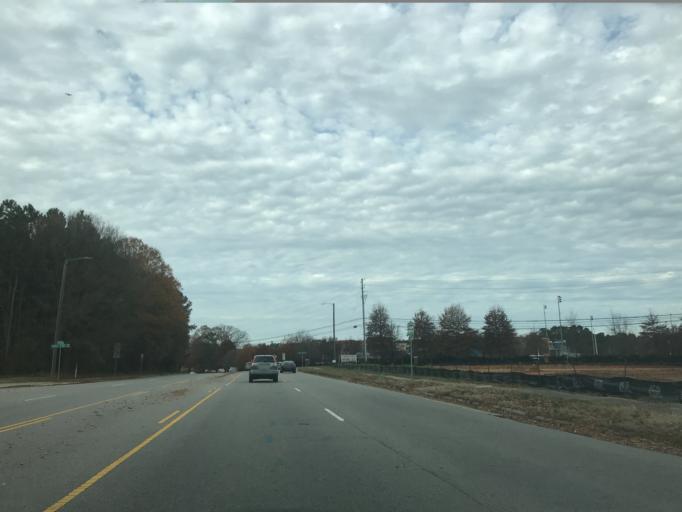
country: US
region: North Carolina
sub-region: Wake County
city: Raleigh
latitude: 35.8624
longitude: -78.6019
